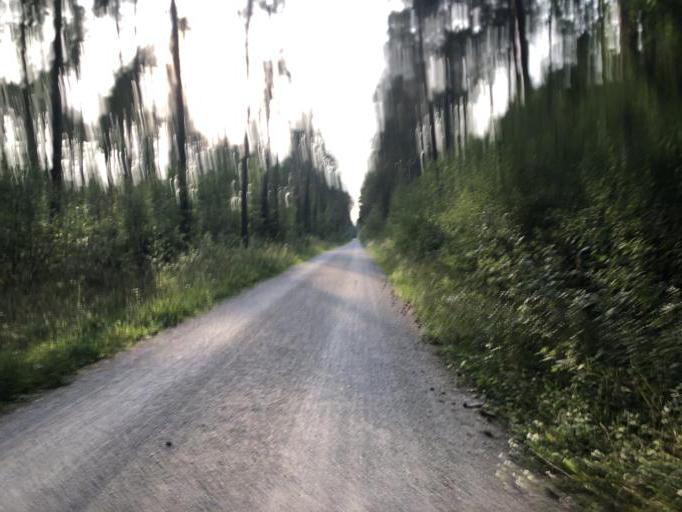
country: DE
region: Bavaria
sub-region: Regierungsbezirk Mittelfranken
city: Buckenhof
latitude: 49.5764
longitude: 11.0539
